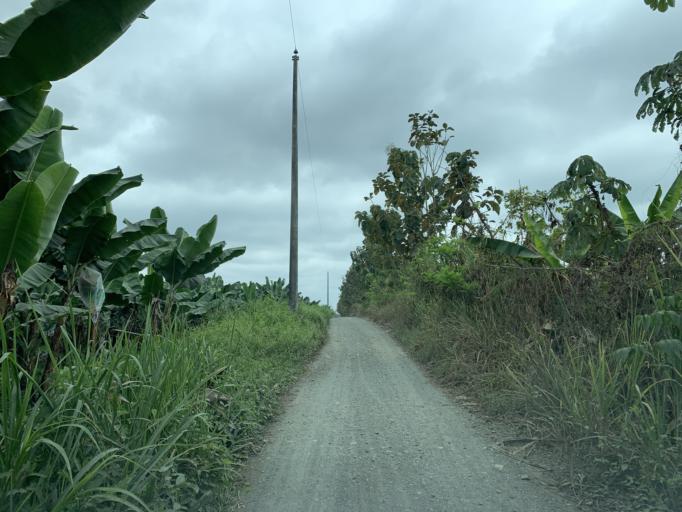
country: EC
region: Guayas
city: Coronel Marcelino Mariduena
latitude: -2.3398
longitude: -79.4572
